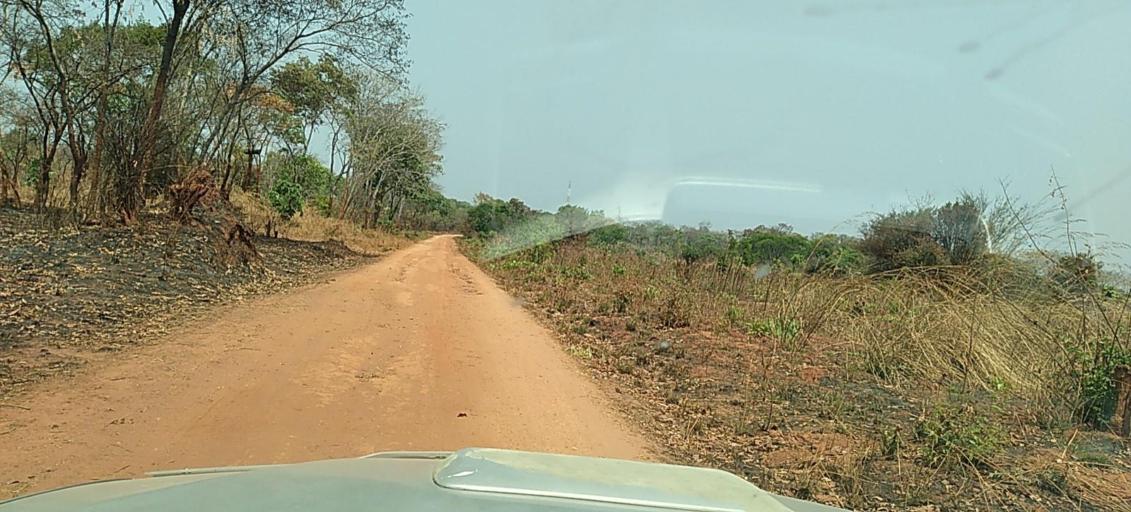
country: ZM
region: North-Western
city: Kasempa
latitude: -13.6826
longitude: 26.3160
